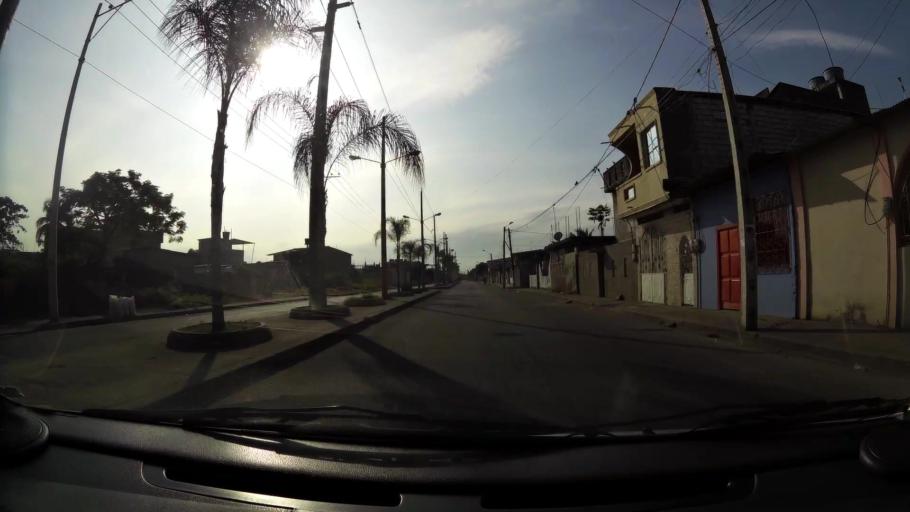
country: EC
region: Guayas
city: Eloy Alfaro
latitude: -2.1822
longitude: -79.8449
